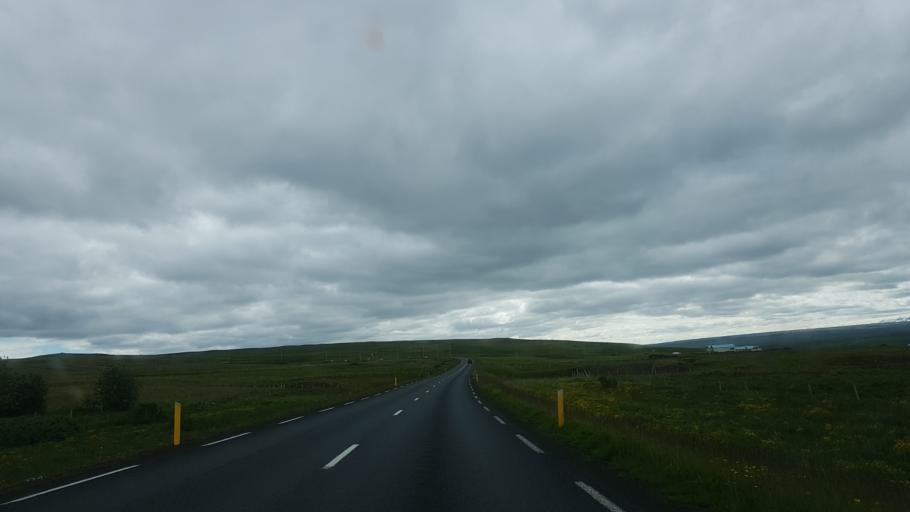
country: IS
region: Northwest
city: Saudarkrokur
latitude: 65.3582
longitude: -20.8895
